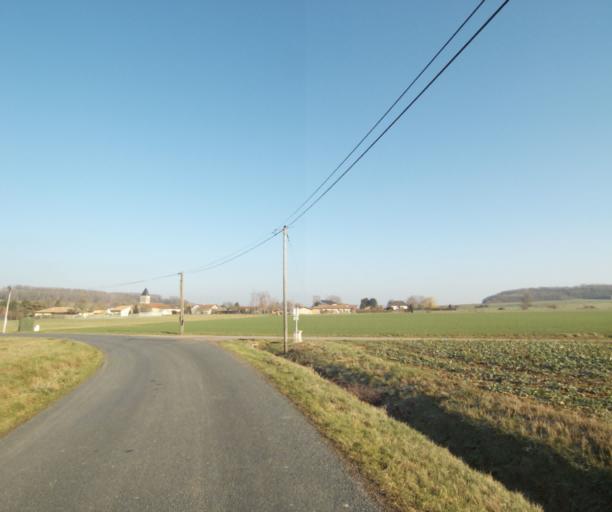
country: FR
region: Champagne-Ardenne
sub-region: Departement de la Haute-Marne
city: Bienville
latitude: 48.5388
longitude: 5.0186
